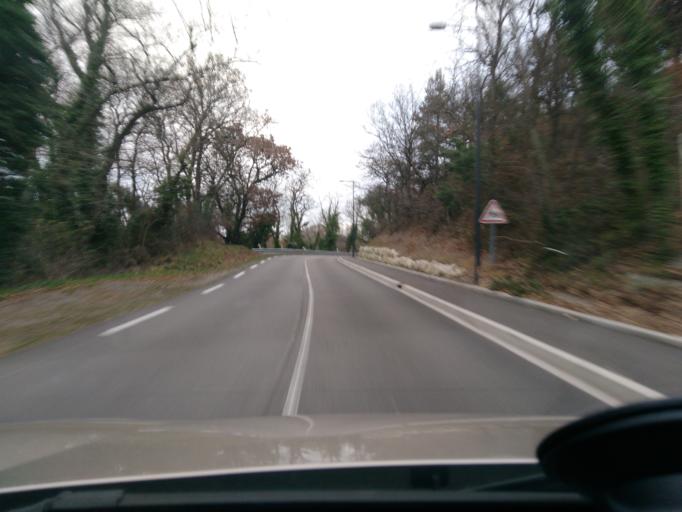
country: FR
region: Rhone-Alpes
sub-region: Departement de la Drome
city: Montelimar
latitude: 44.5599
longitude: 4.7713
